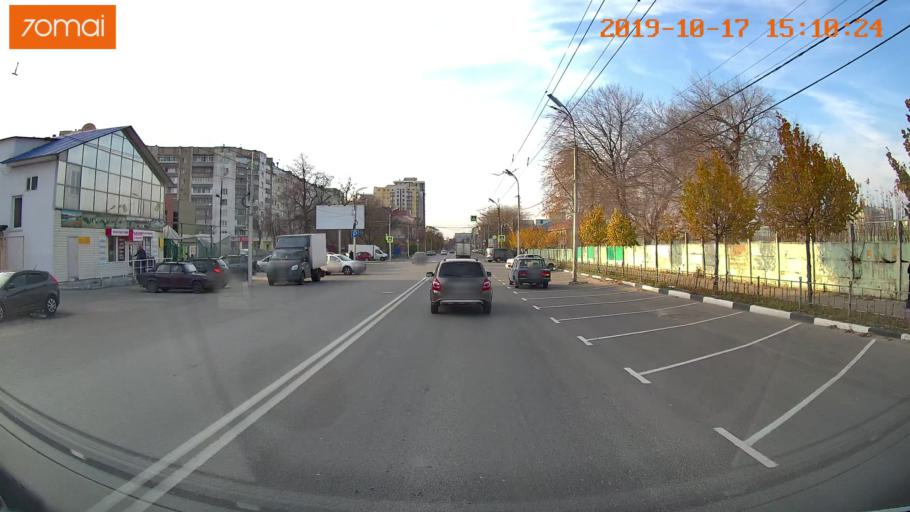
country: RU
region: Rjazan
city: Ryazan'
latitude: 54.6306
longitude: 39.7195
